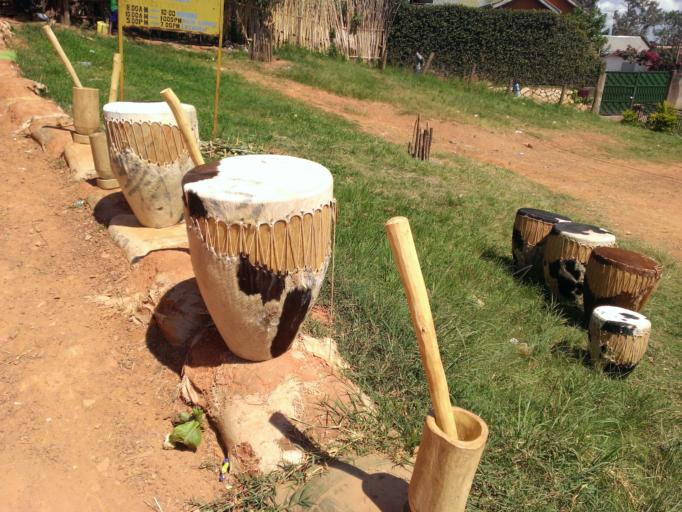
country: UG
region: Central Region
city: Kampala Central Division
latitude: 0.3302
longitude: 32.5534
